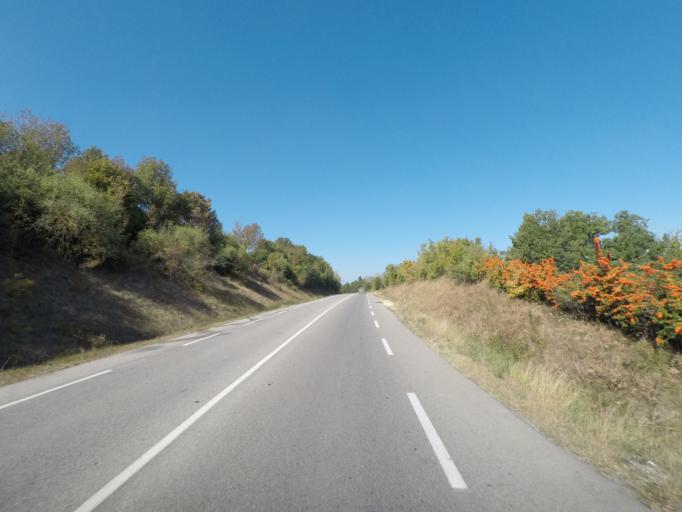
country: FR
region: Rhone-Alpes
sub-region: Departement de la Drome
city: Crest
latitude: 44.7210
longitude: 5.0222
